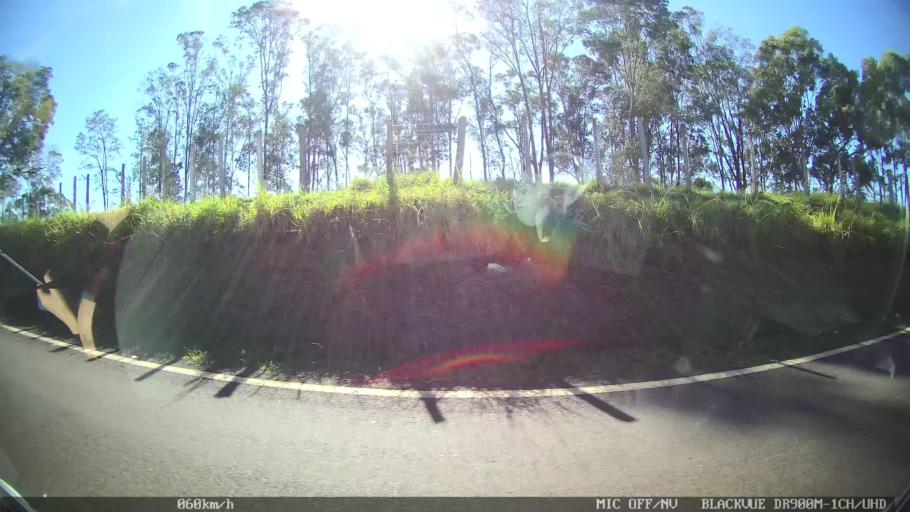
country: BR
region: Sao Paulo
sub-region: Franca
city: Franca
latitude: -20.5865
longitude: -47.3332
